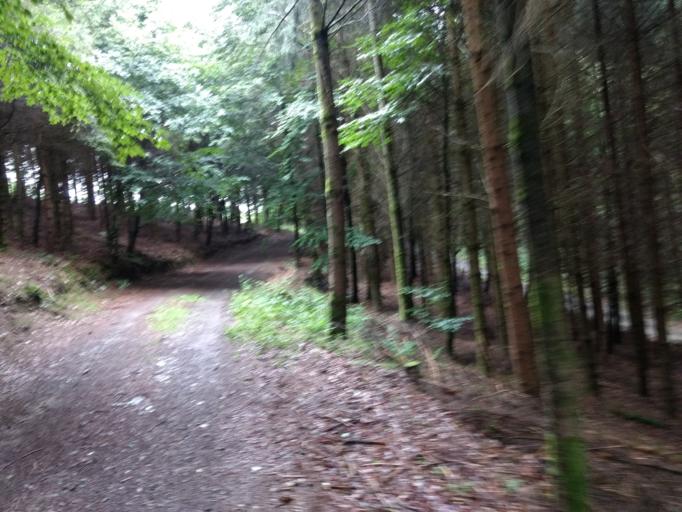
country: BE
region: Wallonia
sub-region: Province du Luxembourg
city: Bertogne
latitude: 50.1426
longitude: 5.7123
